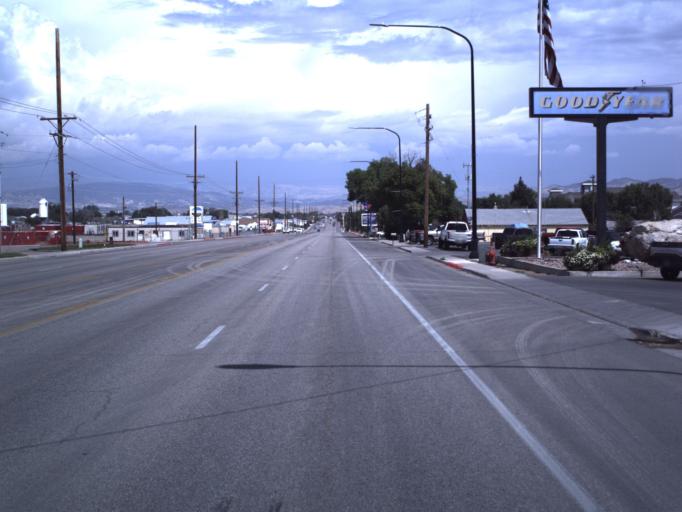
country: US
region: Utah
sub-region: Uintah County
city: Naples
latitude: 40.4255
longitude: -109.4993
